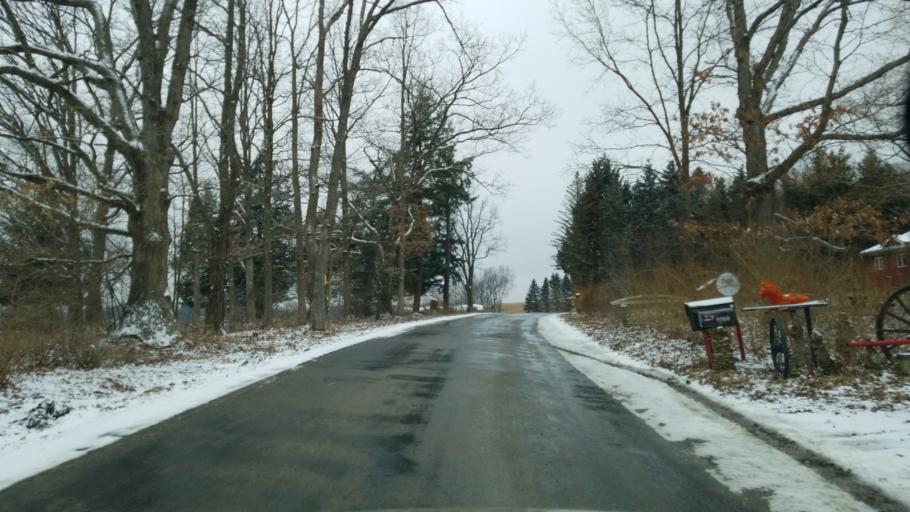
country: US
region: Pennsylvania
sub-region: Jefferson County
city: Sykesville
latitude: 41.0817
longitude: -78.8101
